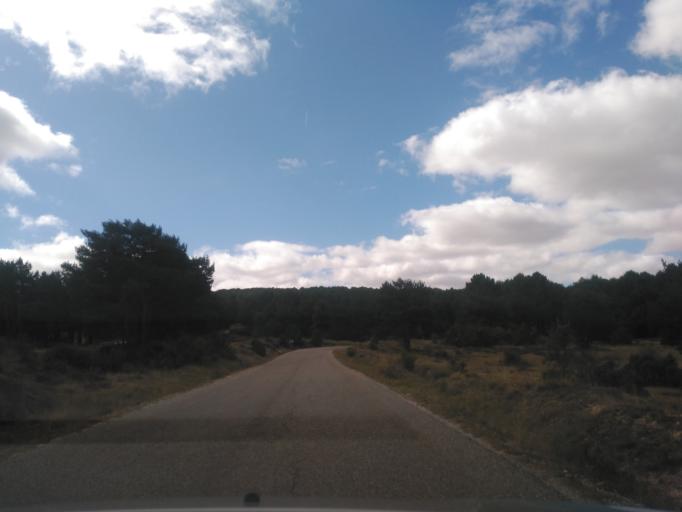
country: ES
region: Castille and Leon
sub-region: Provincia de Soria
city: Espejon
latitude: 41.8483
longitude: -3.2303
